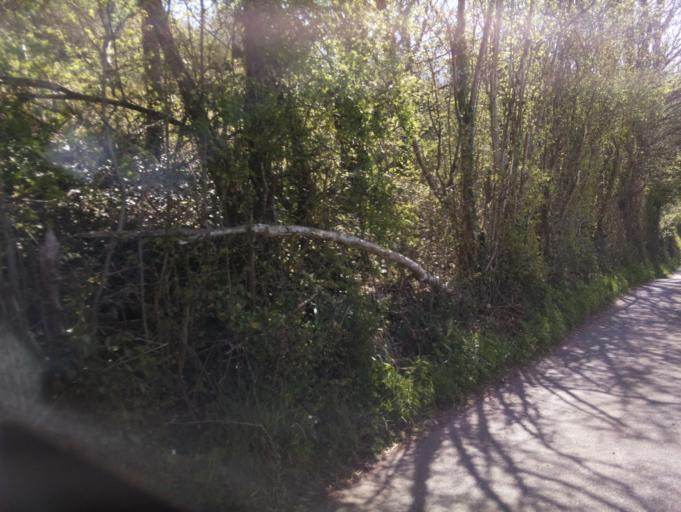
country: GB
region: Wales
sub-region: Monmouthshire
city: Llangwm
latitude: 51.6809
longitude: -2.8111
